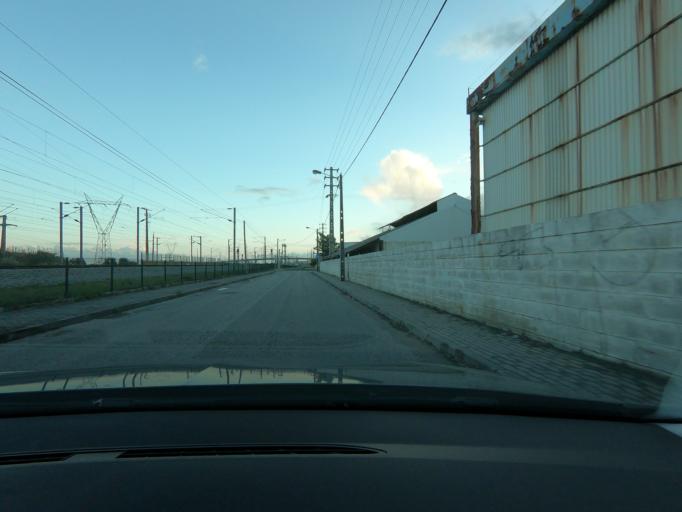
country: PT
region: Lisbon
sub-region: Vila Franca de Xira
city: Castanheira do Ribatejo
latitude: 38.9868
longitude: -8.9672
